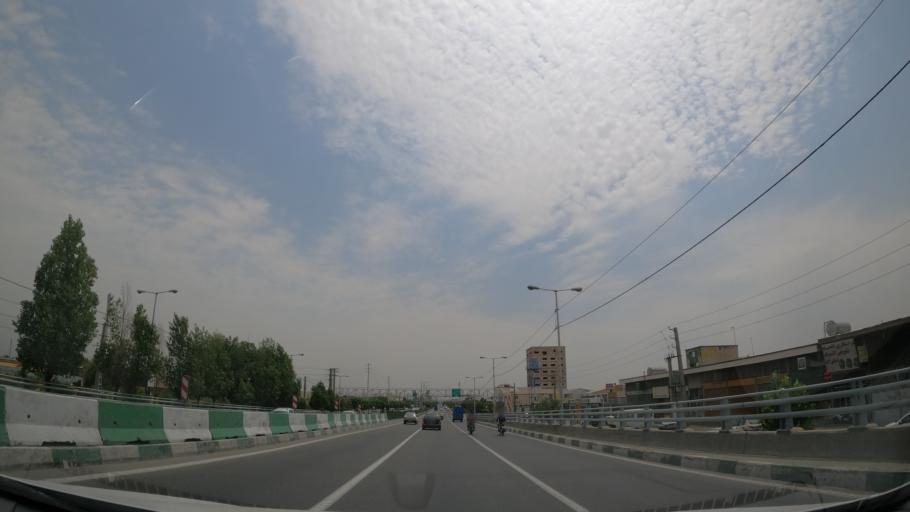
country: IR
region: Tehran
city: Eslamshahr
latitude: 35.6766
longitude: 51.2801
